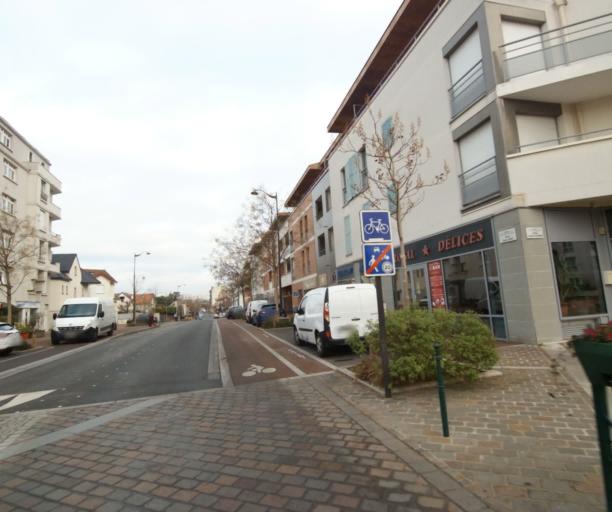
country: FR
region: Ile-de-France
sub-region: Departement des Hauts-de-Seine
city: Rueil-Malmaison
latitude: 48.8671
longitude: 2.2038
